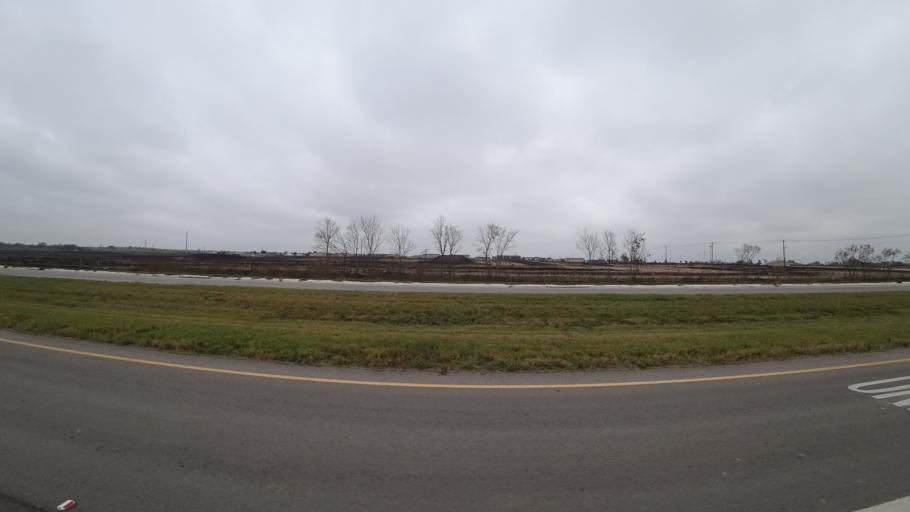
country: US
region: Texas
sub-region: Travis County
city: Pflugerville
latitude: 30.4036
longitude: -97.6074
